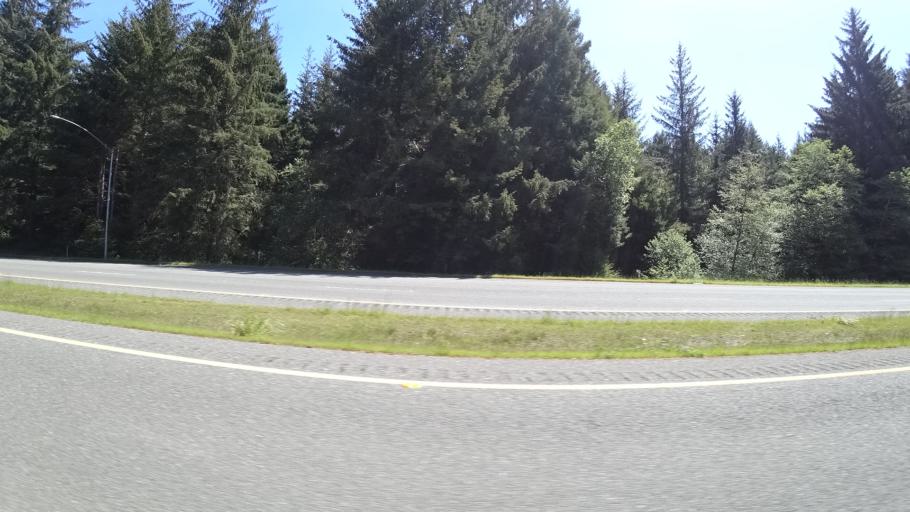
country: US
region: California
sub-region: Humboldt County
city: Westhaven-Moonstone
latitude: 41.1271
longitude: -124.1508
